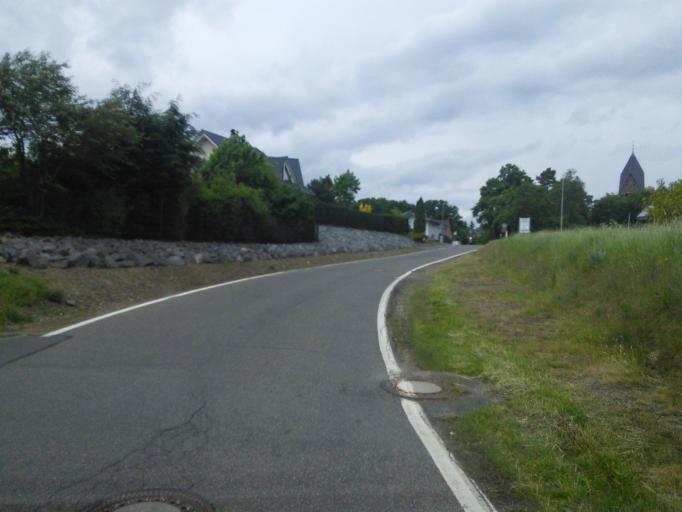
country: DE
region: Rheinland-Pfalz
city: Kirchsahr
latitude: 50.5391
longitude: 6.9057
